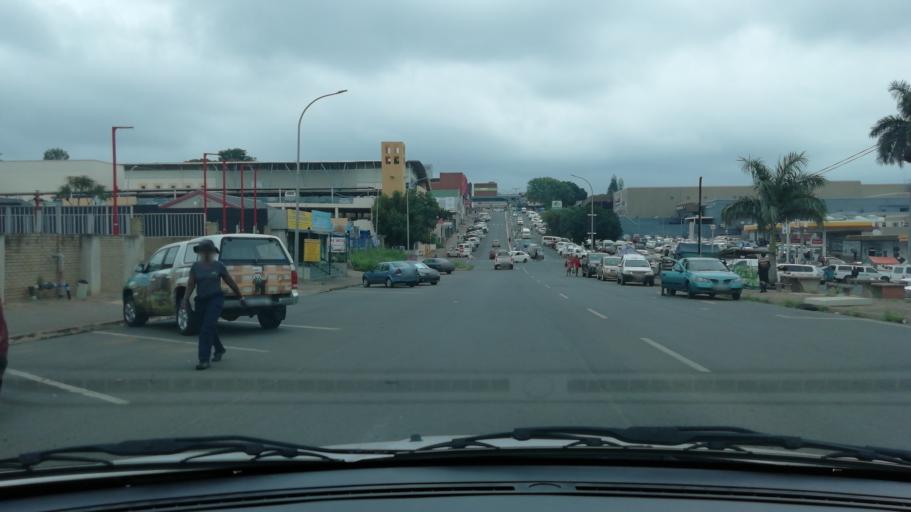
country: ZA
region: KwaZulu-Natal
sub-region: uThungulu District Municipality
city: Empangeni
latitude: -28.7412
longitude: 31.8919
